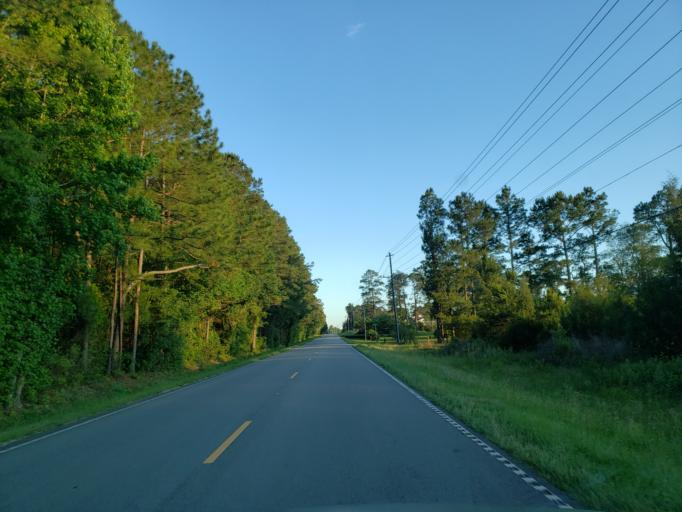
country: US
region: Georgia
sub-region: Lowndes County
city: Valdosta
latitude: 30.7091
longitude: -83.2419
